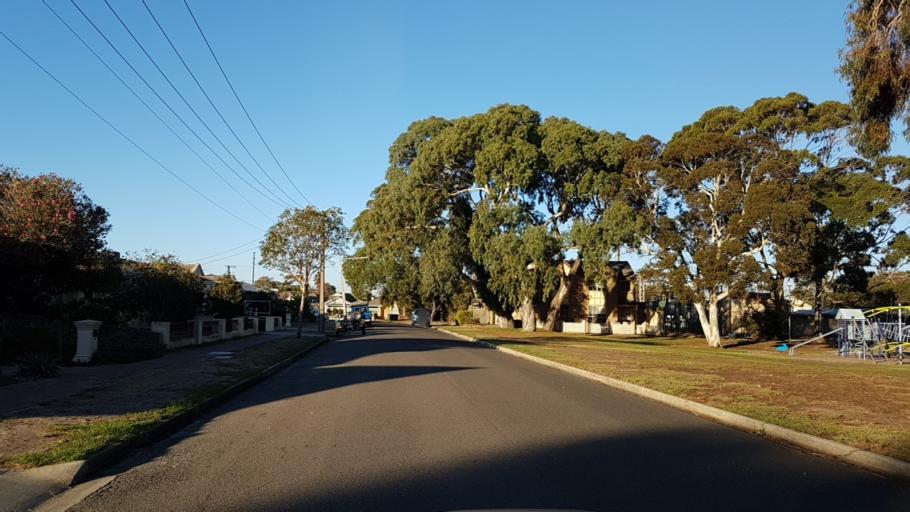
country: AU
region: South Australia
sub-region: Charles Sturt
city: Henley Beach
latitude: -34.9292
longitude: 138.5055
